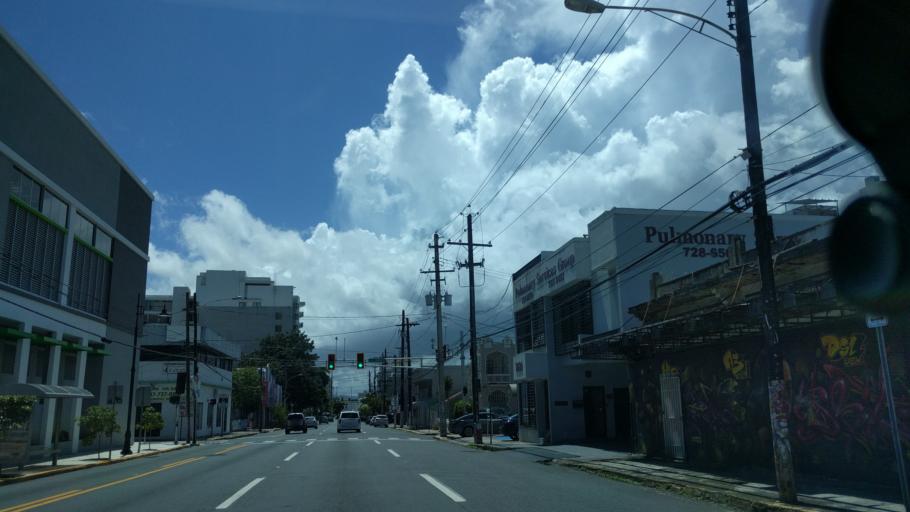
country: PR
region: San Juan
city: San Juan
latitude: 18.4394
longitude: -66.0618
